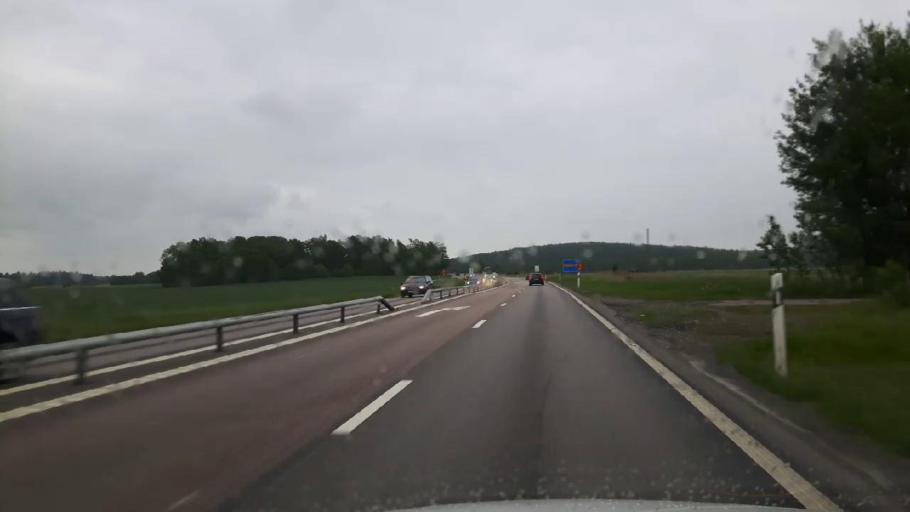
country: SE
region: Vaestmanland
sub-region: Arboga Kommun
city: Tyringe
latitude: 59.3973
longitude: 15.9082
